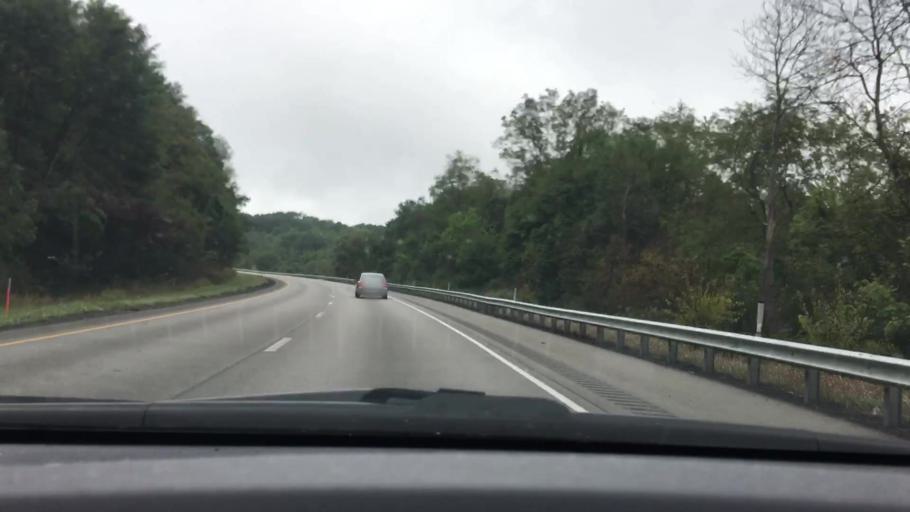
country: US
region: Pennsylvania
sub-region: Butler County
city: Evans City
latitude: 40.7511
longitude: -80.1070
